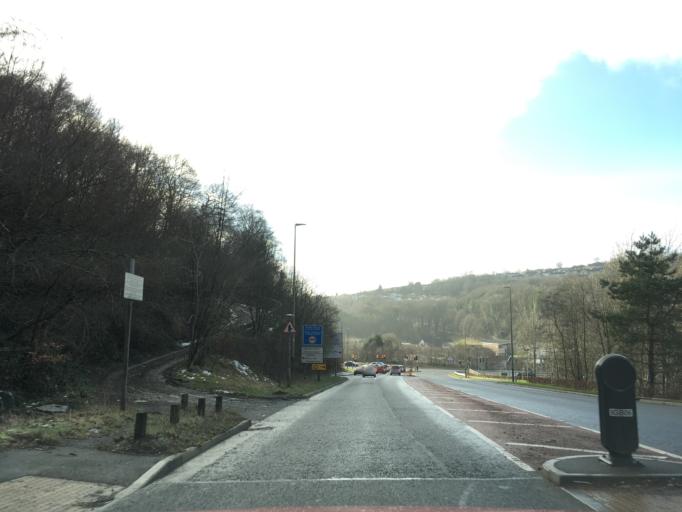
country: GB
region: Wales
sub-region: Caerphilly County Borough
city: Crumlin
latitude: 51.6797
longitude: -3.1363
